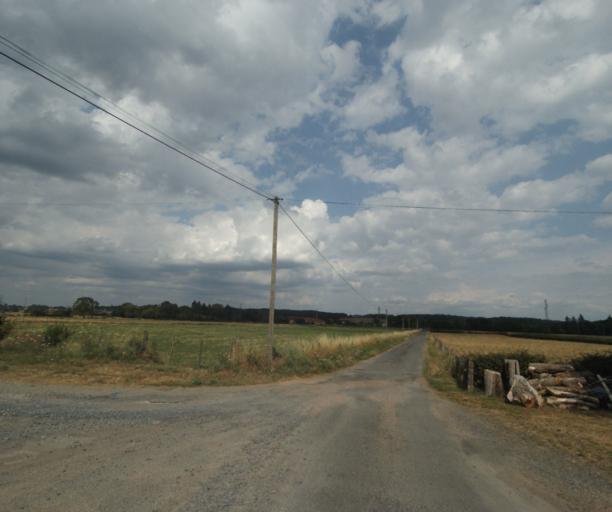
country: FR
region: Bourgogne
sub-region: Departement de Saone-et-Loire
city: Gueugnon
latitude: 46.6124
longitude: 4.0695
